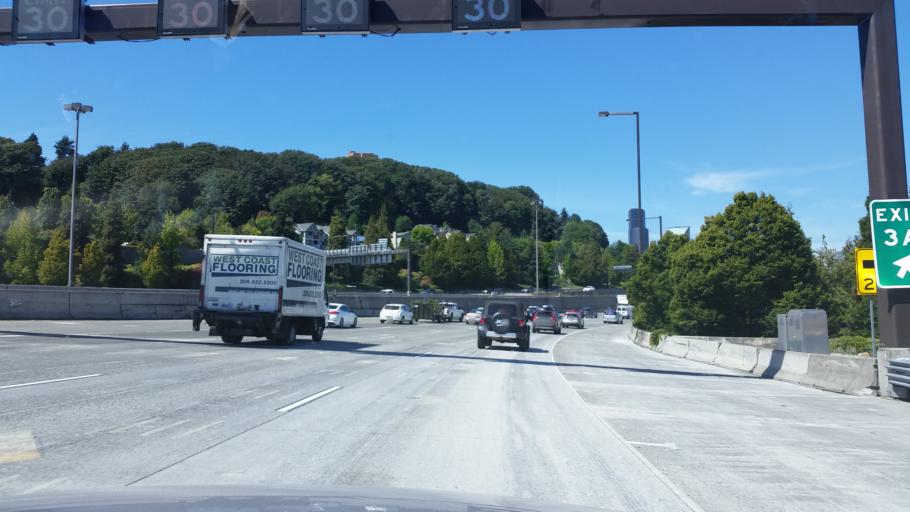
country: US
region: Washington
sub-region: King County
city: Seattle
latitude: 47.5909
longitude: -122.3093
